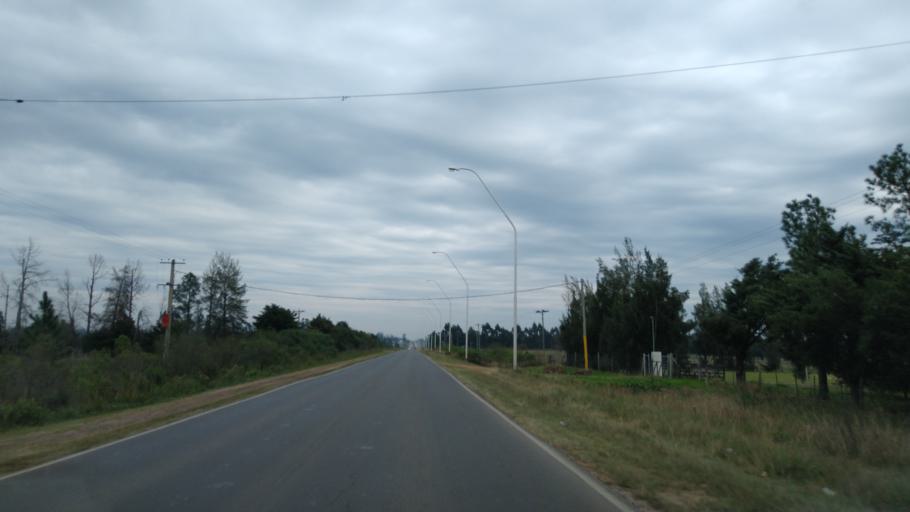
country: AR
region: Entre Rios
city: Villa del Rosario
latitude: -30.7856
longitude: -57.9488
